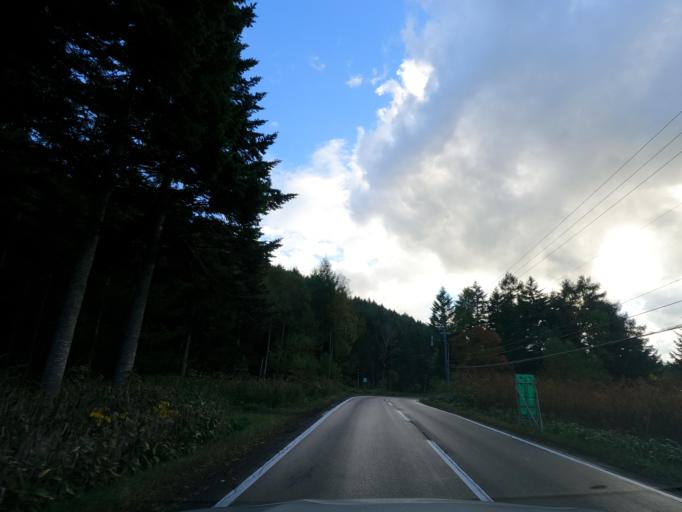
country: JP
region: Hokkaido
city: Shiraoi
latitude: 42.6834
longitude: 141.1016
